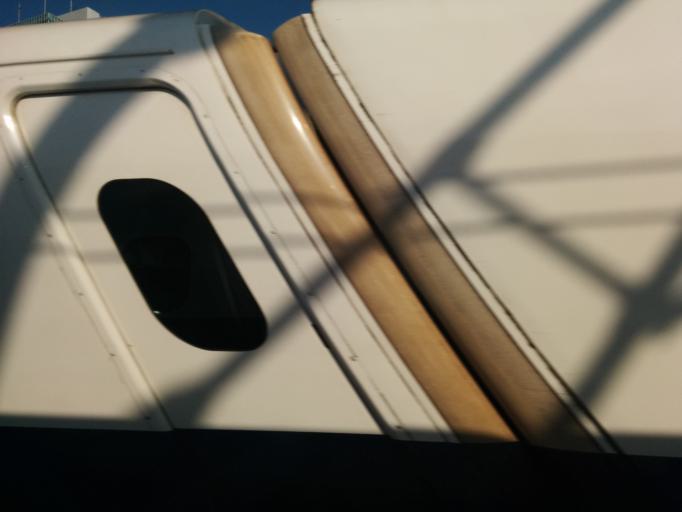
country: JP
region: Aichi
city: Nagoya-shi
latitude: 35.1639
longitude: 136.8852
